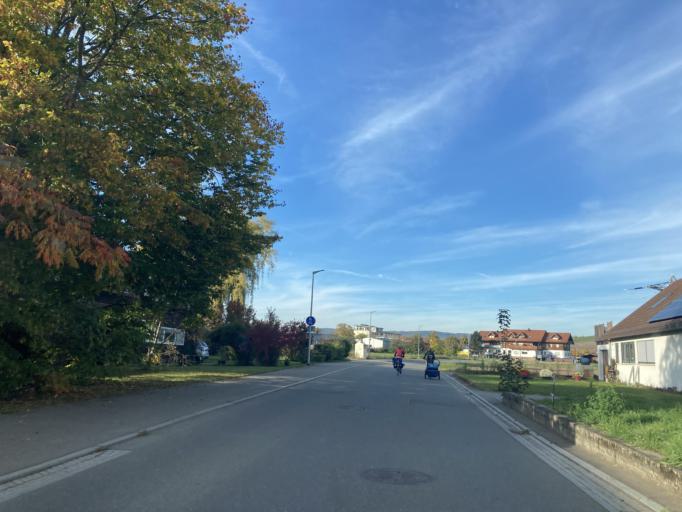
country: DE
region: Baden-Wuerttemberg
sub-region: Tuebingen Region
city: Rottenburg
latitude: 48.5277
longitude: 8.9647
